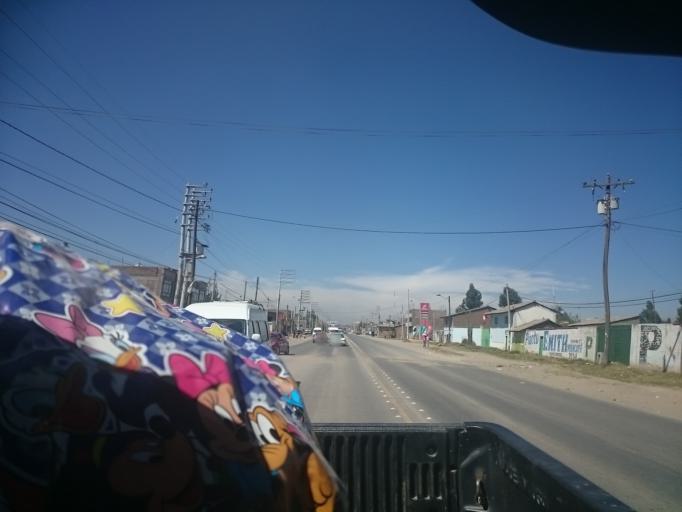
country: PE
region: Junin
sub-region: Provincia de Huancayo
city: Hualhuas
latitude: -12.0077
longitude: -75.2481
